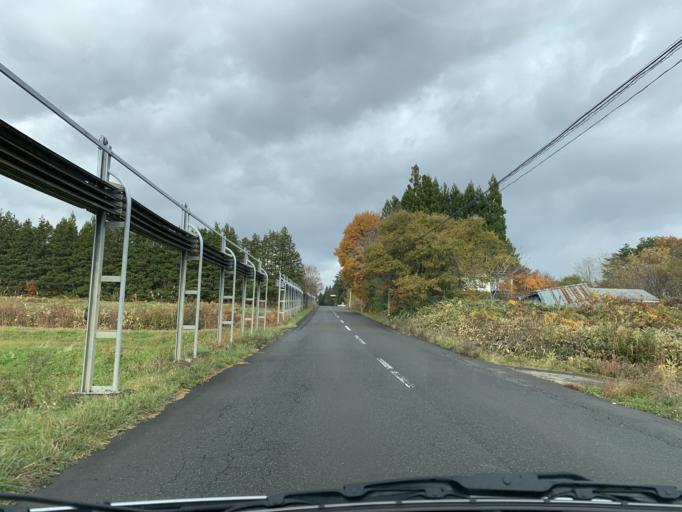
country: JP
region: Iwate
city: Mizusawa
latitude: 39.1095
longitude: 140.9881
